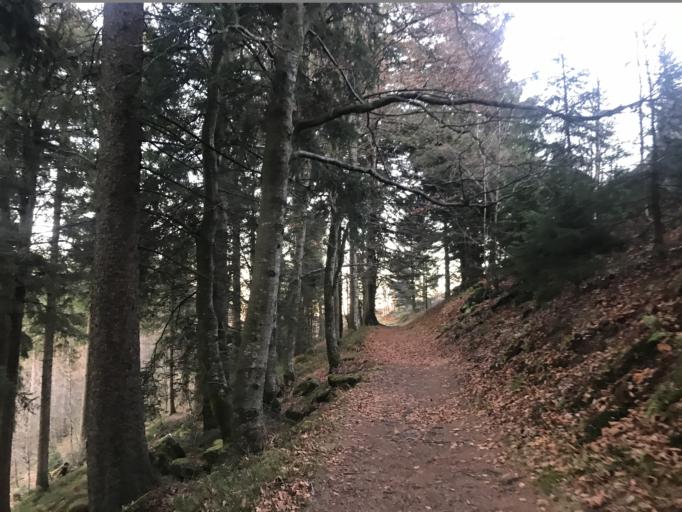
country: DE
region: Baden-Wuerttemberg
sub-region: Freiburg Region
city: Glottertal
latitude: 48.0633
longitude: 8.0133
